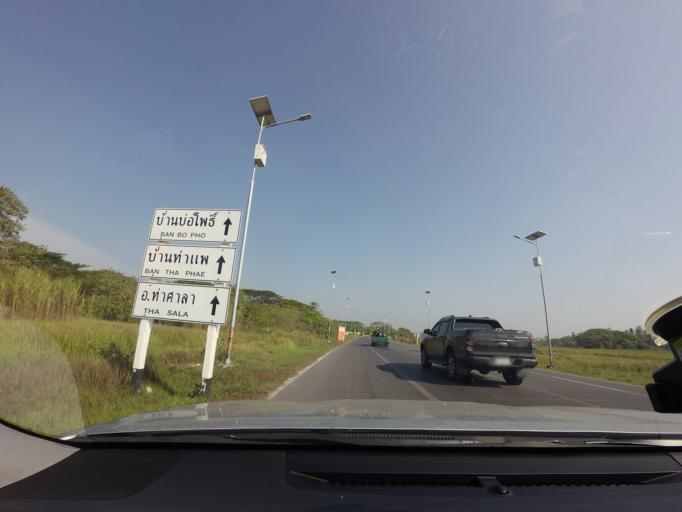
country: TH
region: Nakhon Si Thammarat
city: Nakhon Si Thammarat
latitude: 8.4541
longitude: 99.9799
